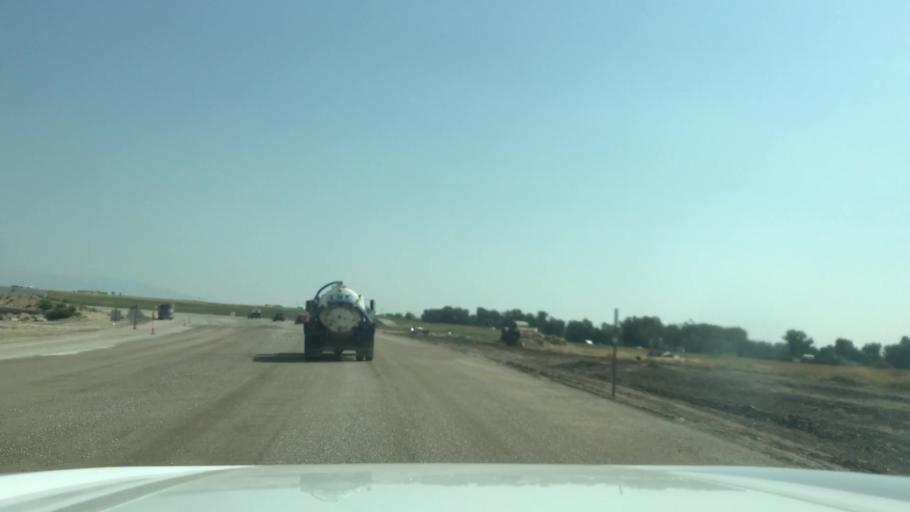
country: US
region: Montana
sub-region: Judith Basin County
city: Stanford
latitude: 47.0068
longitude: -109.8709
